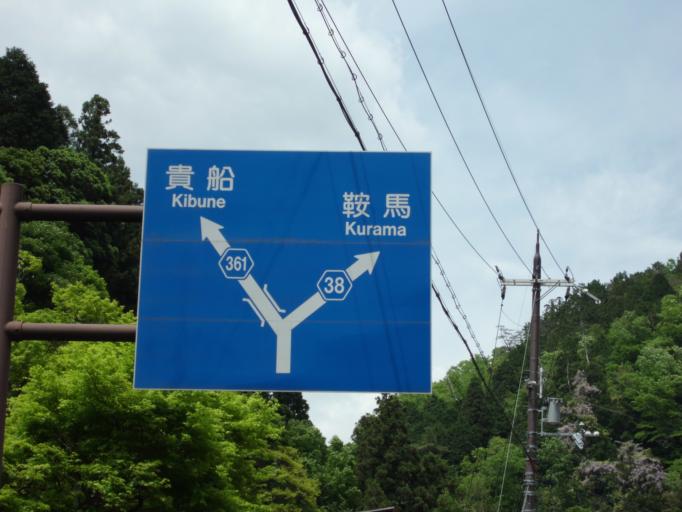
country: JP
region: Kyoto
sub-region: Kyoto-shi
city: Kamigyo-ku
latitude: 35.1043
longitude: 135.7630
